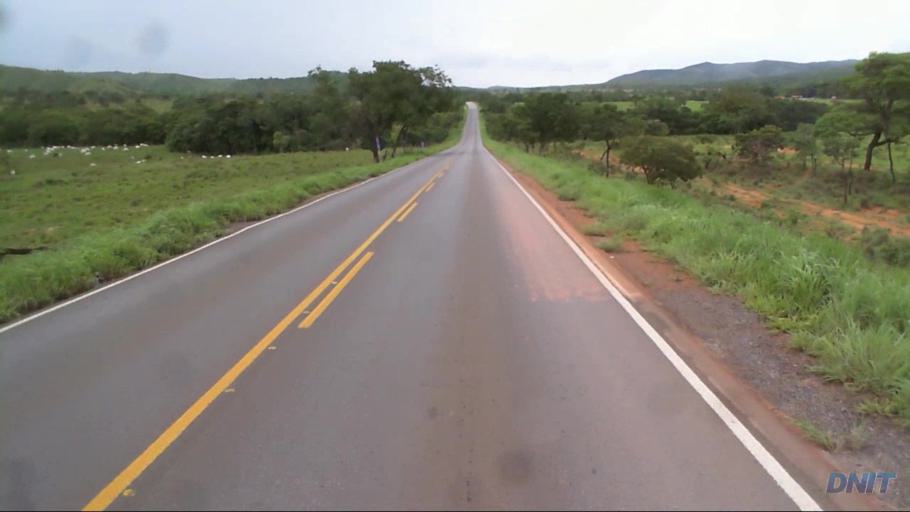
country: BR
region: Goias
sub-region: Padre Bernardo
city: Padre Bernardo
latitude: -15.4412
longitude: -48.1969
